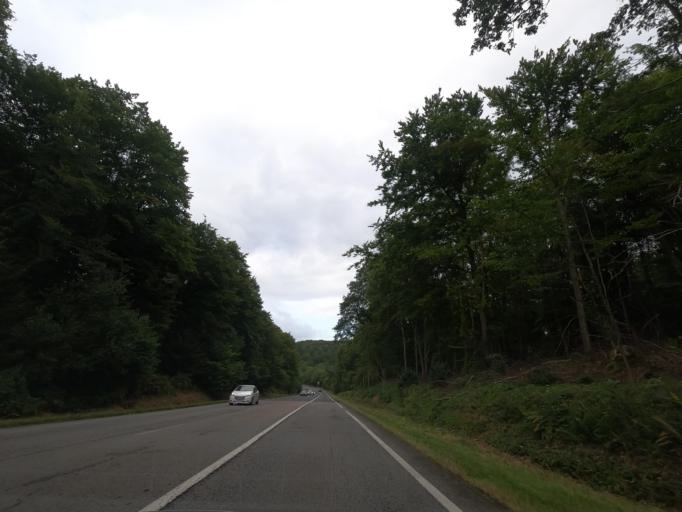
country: FR
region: Haute-Normandie
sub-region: Departement de la Seine-Maritime
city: Sahurs
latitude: 49.3316
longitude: 0.9165
